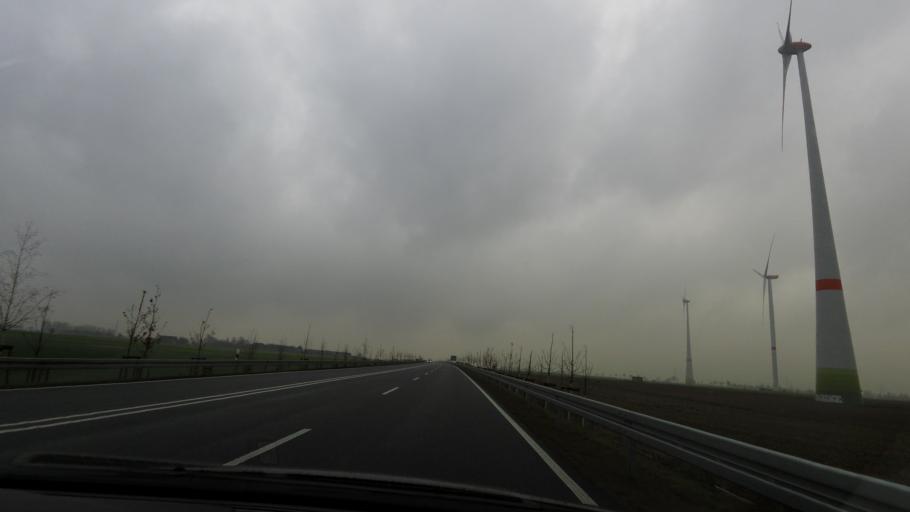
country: DE
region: North Rhine-Westphalia
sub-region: Regierungsbezirk Koln
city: Heinsberg
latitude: 51.0224
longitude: 6.1003
